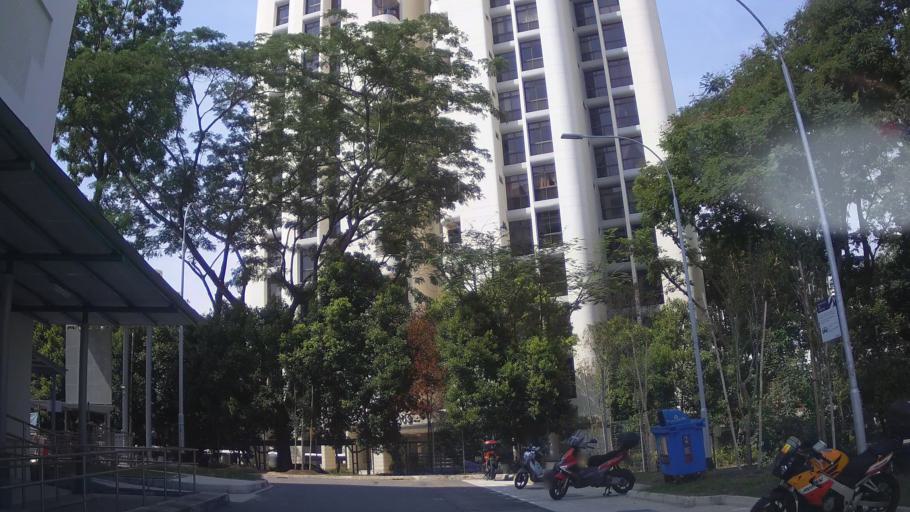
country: MY
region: Johor
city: Johor Bahru
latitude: 1.3741
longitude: 103.7683
